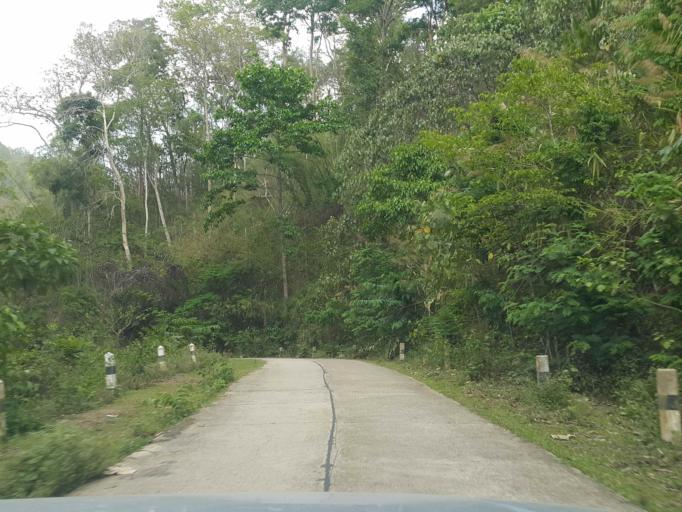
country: TH
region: Chiang Mai
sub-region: Amphoe Chiang Dao
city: Chiang Dao
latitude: 19.3749
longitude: 98.7569
